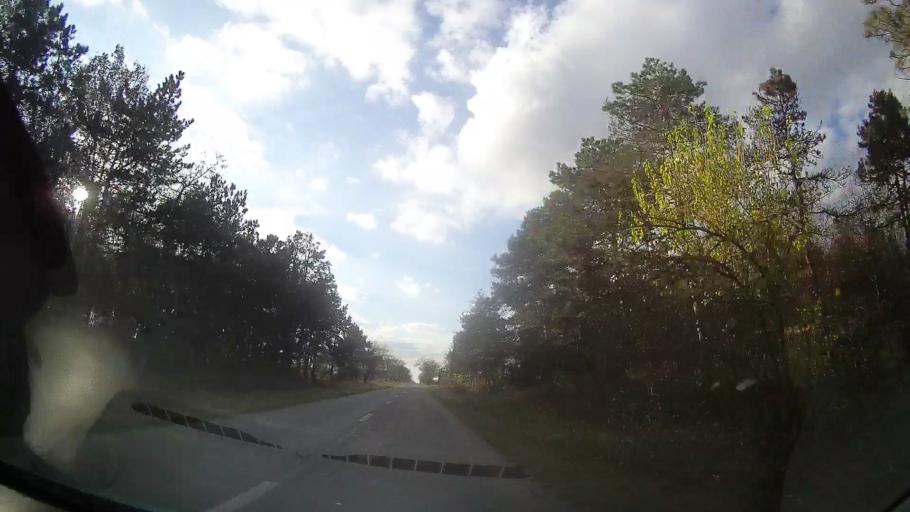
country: RO
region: Constanta
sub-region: Comuna Negru Voda
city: Negru Voda
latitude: 43.8194
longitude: 28.2343
